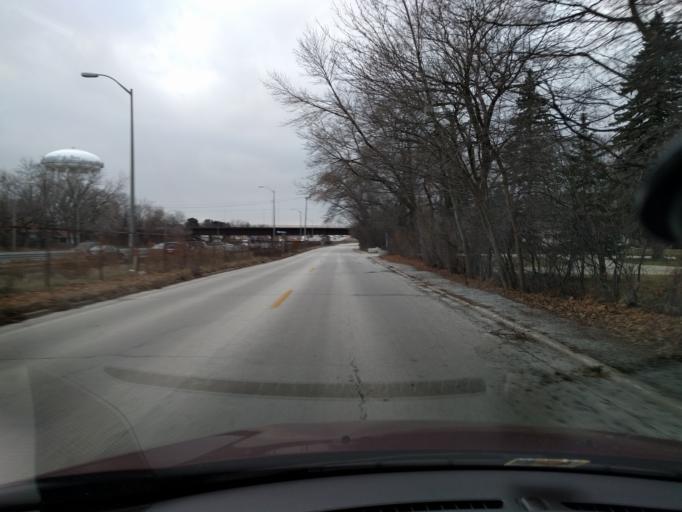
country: US
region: Wisconsin
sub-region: Milwaukee County
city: Glendale
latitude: 43.1341
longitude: -87.9138
